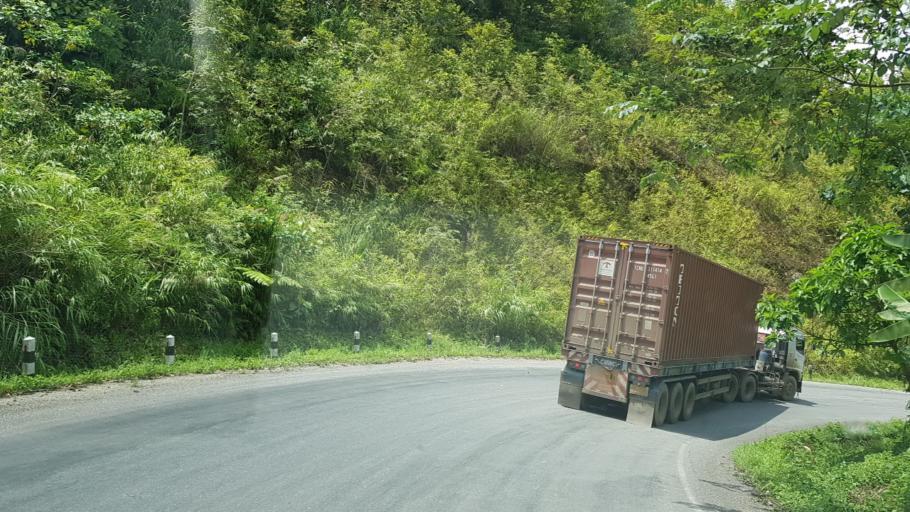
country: LA
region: Vientiane
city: Muang Kasi
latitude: 19.3688
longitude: 102.1610
